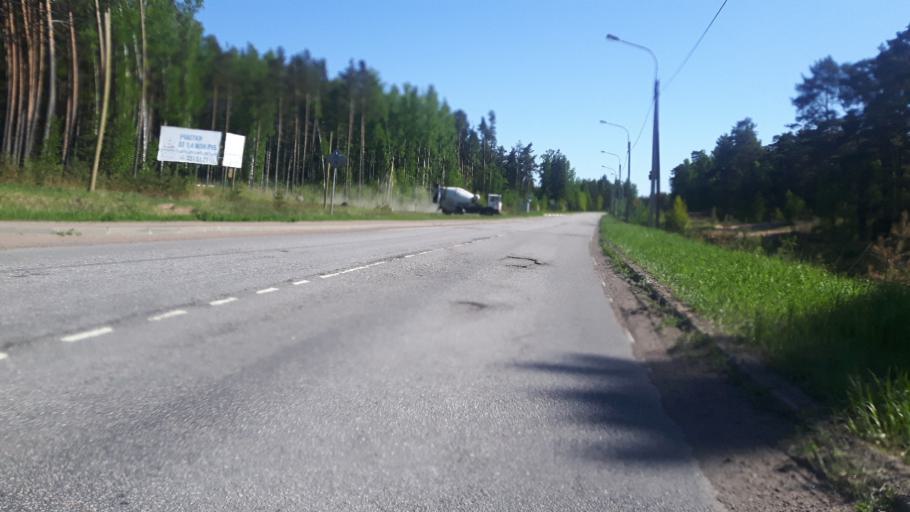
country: RU
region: Leningrad
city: Sosnovyy Bor
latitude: 60.2005
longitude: 29.0069
